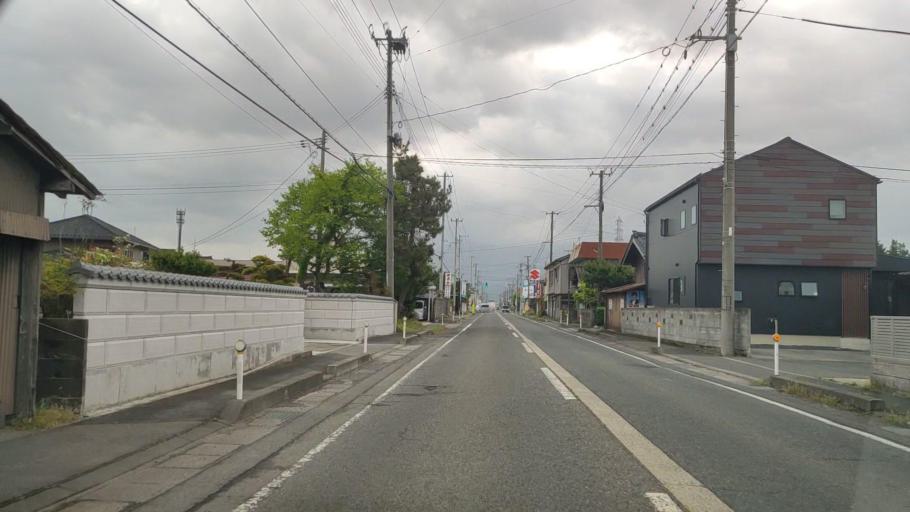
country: JP
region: Niigata
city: Gosen
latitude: 37.7354
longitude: 139.1920
